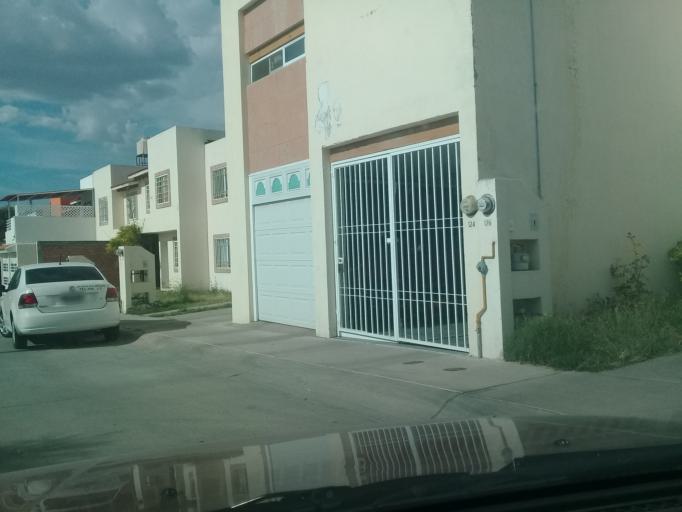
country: MX
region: Aguascalientes
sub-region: Aguascalientes
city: La Loma de los Negritos
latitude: 21.8433
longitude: -102.3190
